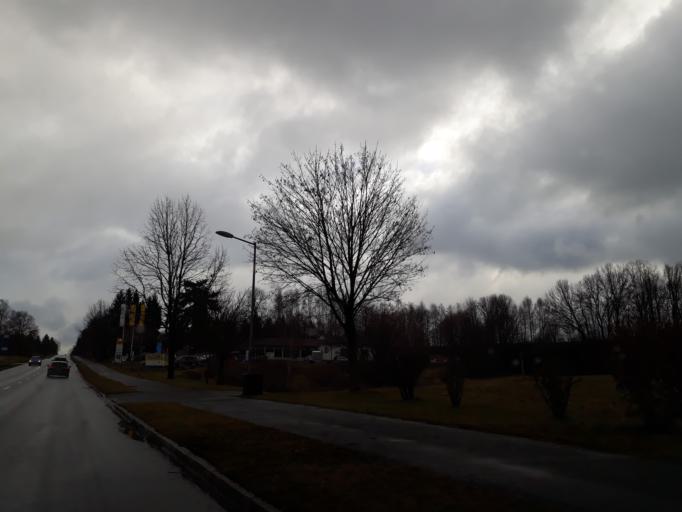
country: DE
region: Saxony
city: Herrnhut
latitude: 51.0272
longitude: 14.7256
